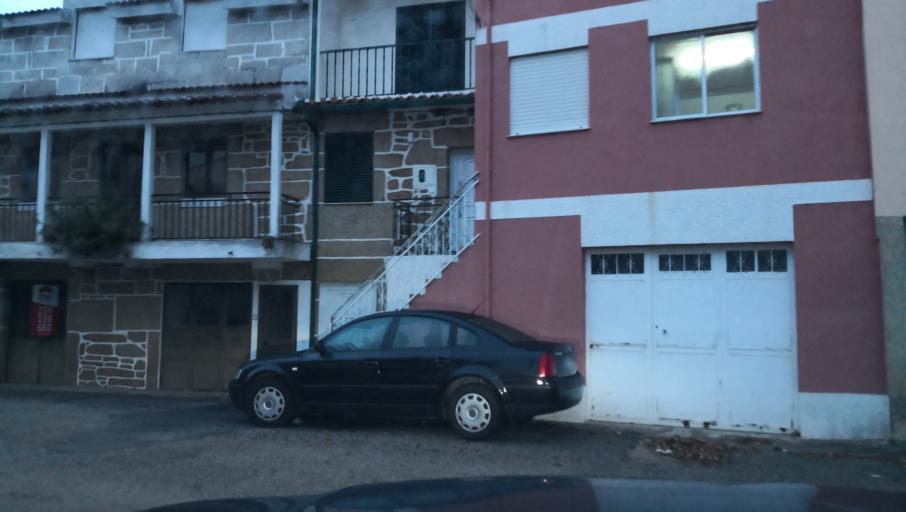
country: PT
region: Vila Real
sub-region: Sabrosa
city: Sabrosa
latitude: 41.2677
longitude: -7.6185
